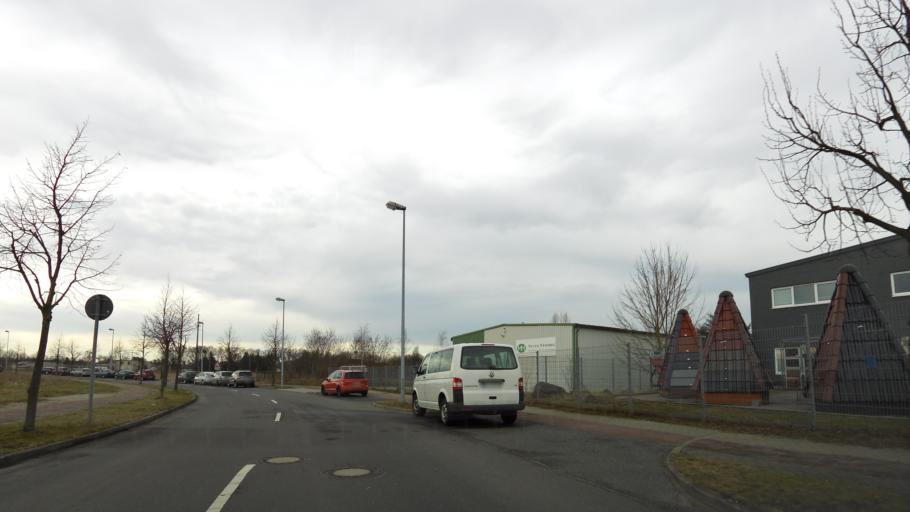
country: DE
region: Brandenburg
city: Strausberg
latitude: 52.5877
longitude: 13.9098
